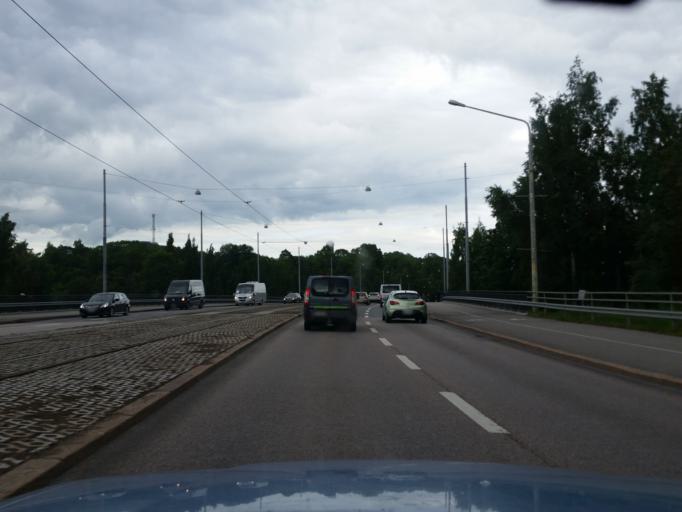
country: FI
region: Uusimaa
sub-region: Helsinki
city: Helsinki
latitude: 60.1994
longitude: 24.9620
